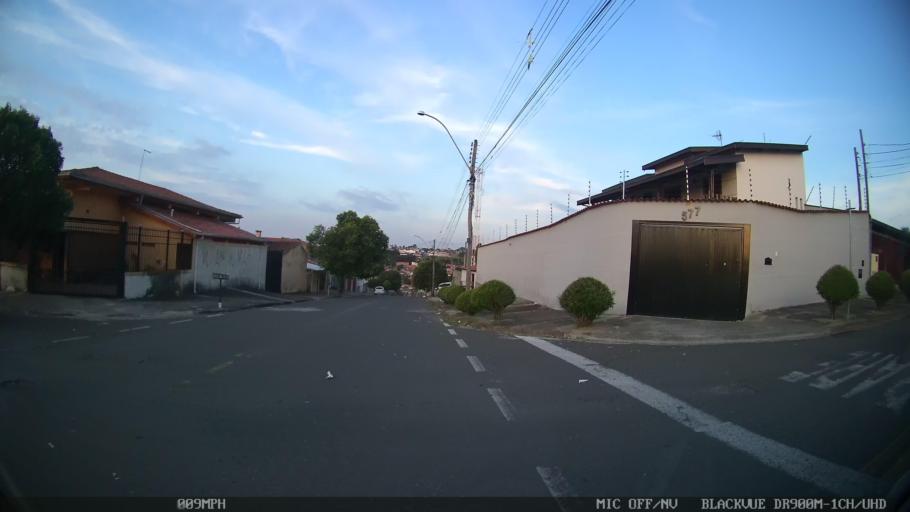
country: BR
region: Sao Paulo
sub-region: Campinas
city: Campinas
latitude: -22.9725
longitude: -47.1210
